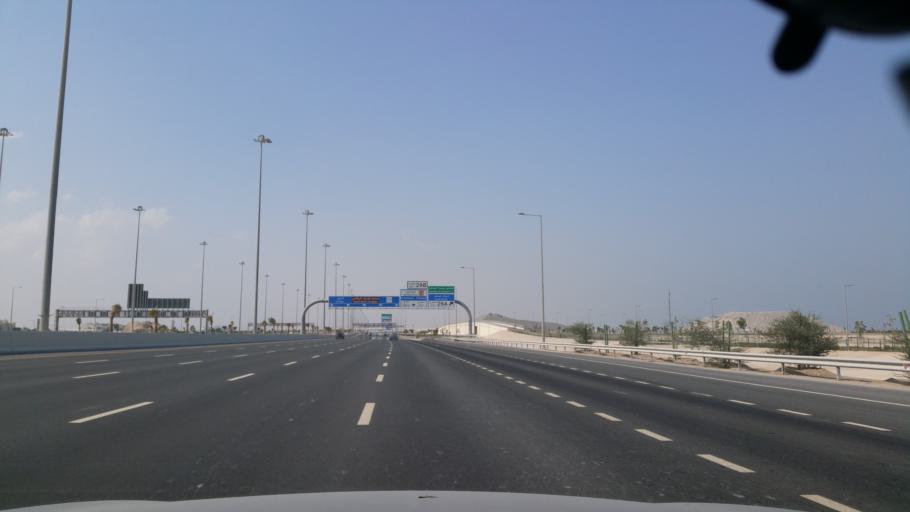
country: QA
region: Baladiyat Umm Salal
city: Umm Salal Muhammad
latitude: 25.4428
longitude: 51.4817
